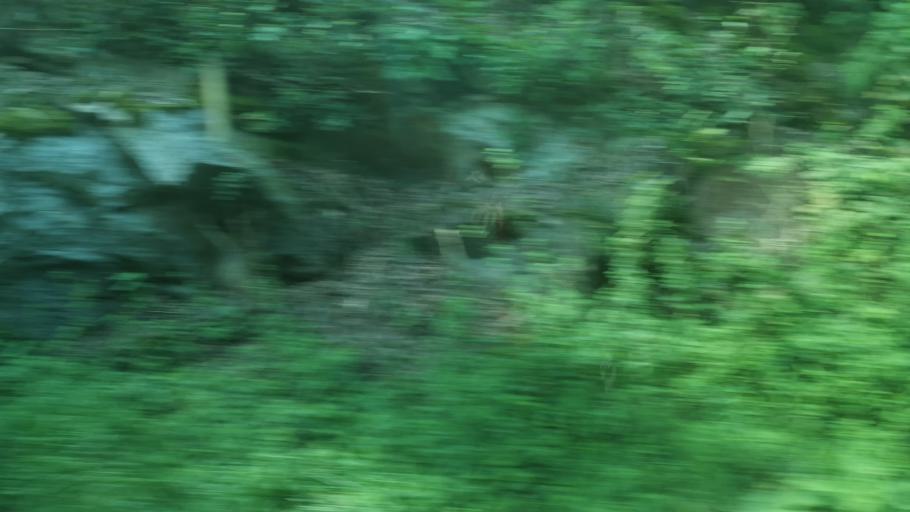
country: DE
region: Bavaria
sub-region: Upper Palatinate
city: Chamerau
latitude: 49.1877
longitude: 12.7330
